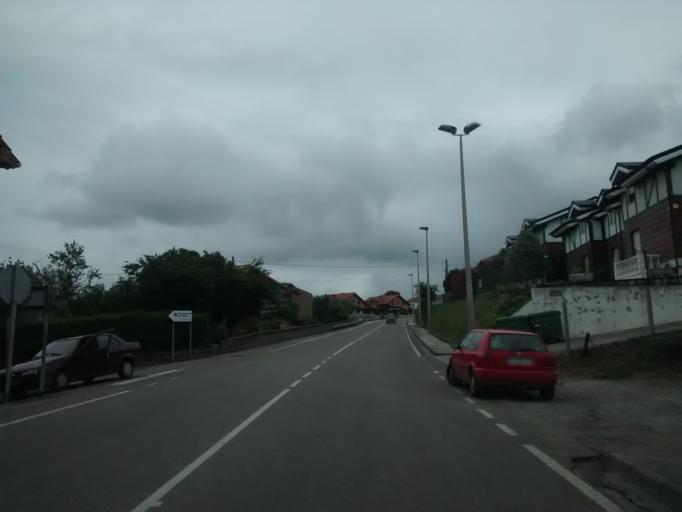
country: ES
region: Cantabria
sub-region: Provincia de Cantabria
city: Polanco
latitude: 43.3906
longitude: -4.0475
